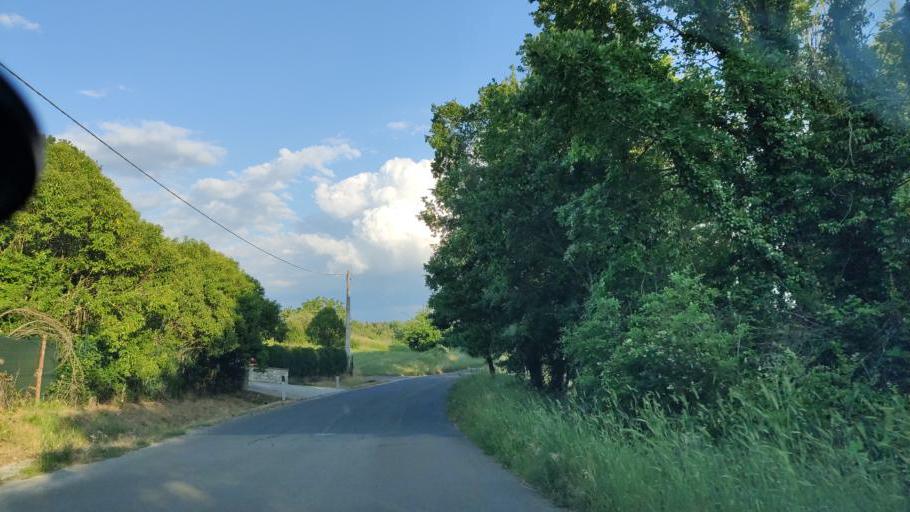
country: IT
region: Umbria
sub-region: Provincia di Terni
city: Lugnano in Teverina
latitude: 42.5943
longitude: 12.3734
